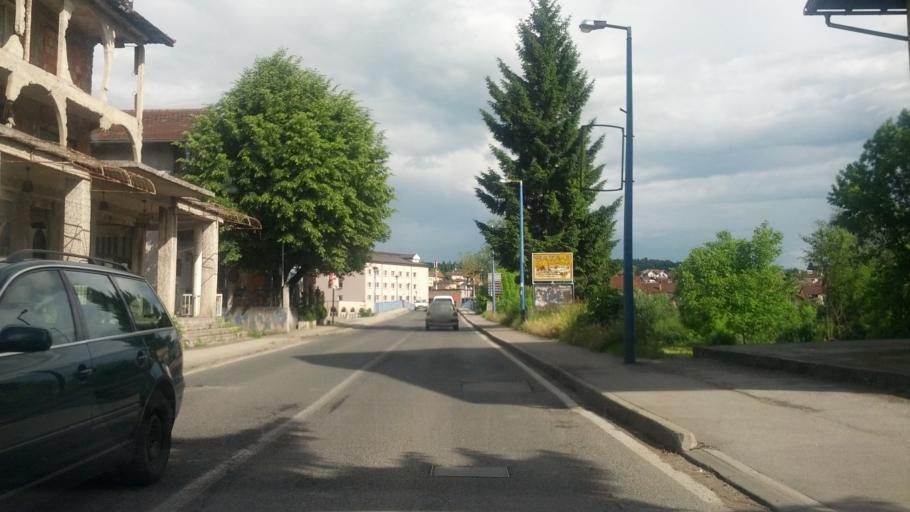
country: BA
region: Federation of Bosnia and Herzegovina
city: Bosanska Krupa
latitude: 44.8859
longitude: 16.1517
